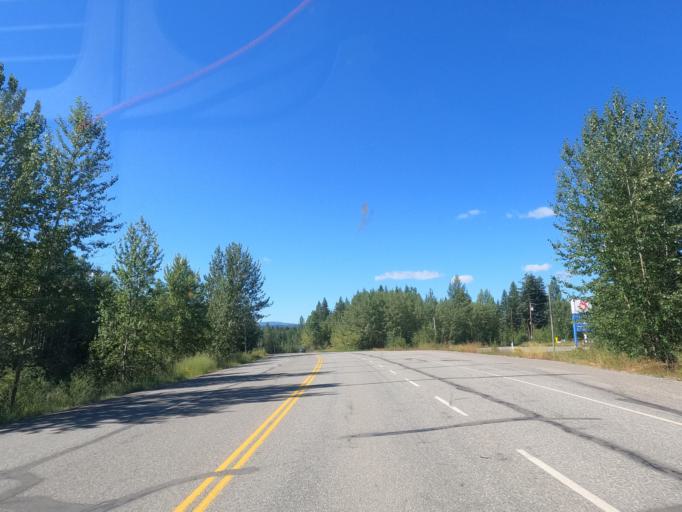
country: CA
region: British Columbia
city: Quesnel
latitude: 53.0191
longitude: -122.4753
